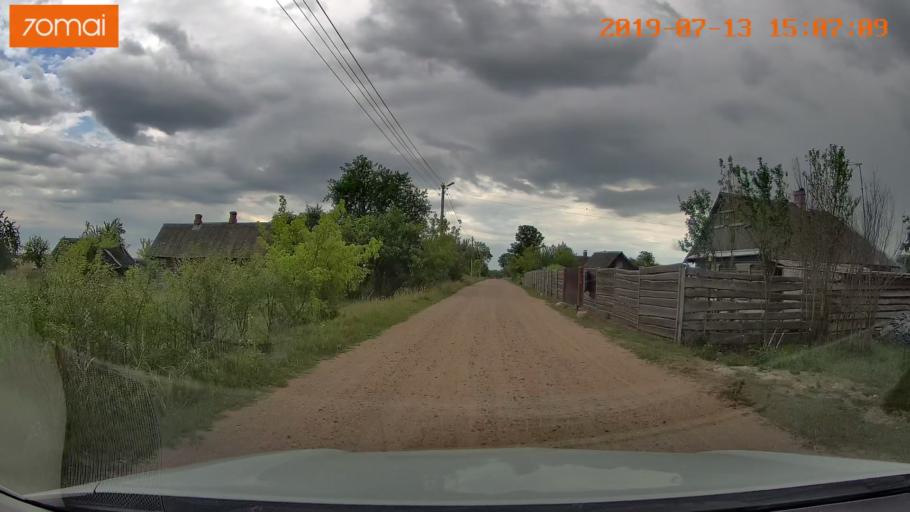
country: BY
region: Mogilev
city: Hlusha
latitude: 53.1928
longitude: 28.7566
